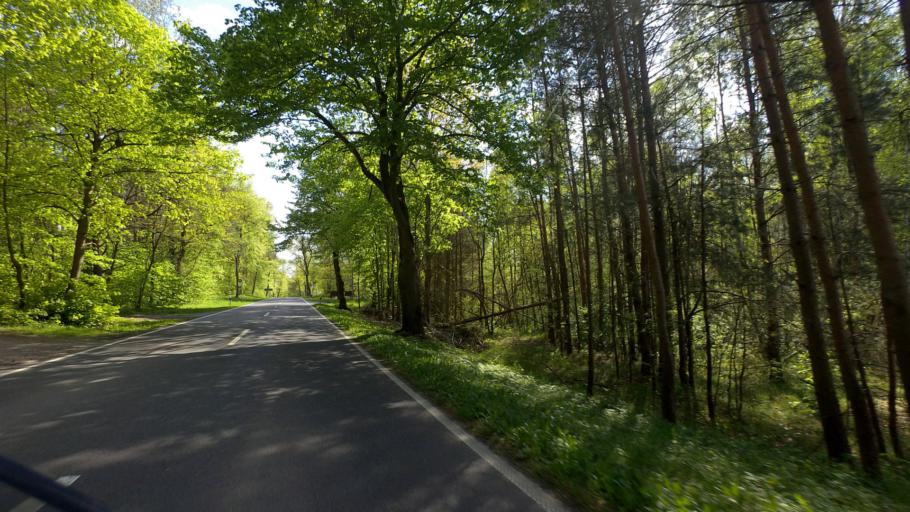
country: DE
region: Brandenburg
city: Templin
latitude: 53.0872
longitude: 13.5070
